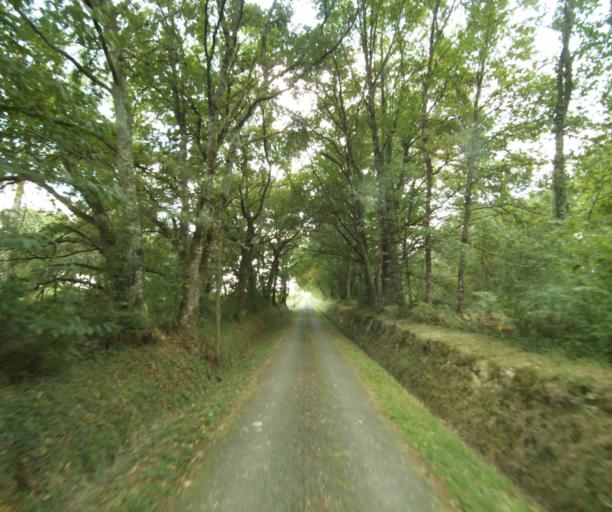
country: FR
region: Midi-Pyrenees
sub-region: Departement du Gers
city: Cazaubon
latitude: 43.8937
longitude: -0.0473
